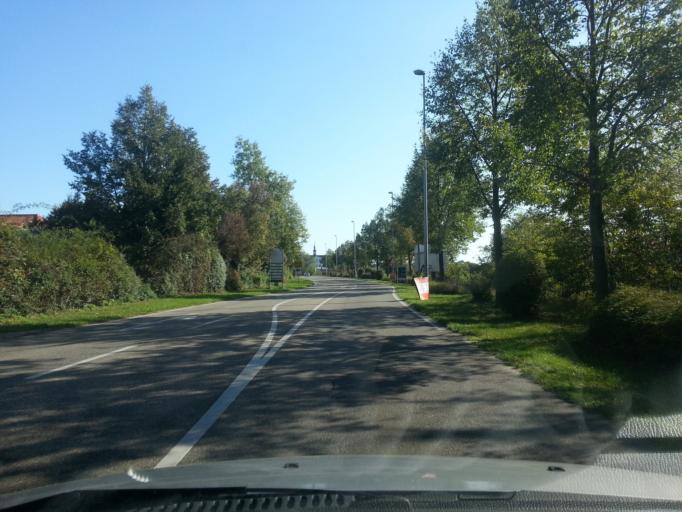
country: DE
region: Rheinland-Pfalz
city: Hassloch
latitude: 49.3569
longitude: 8.2696
